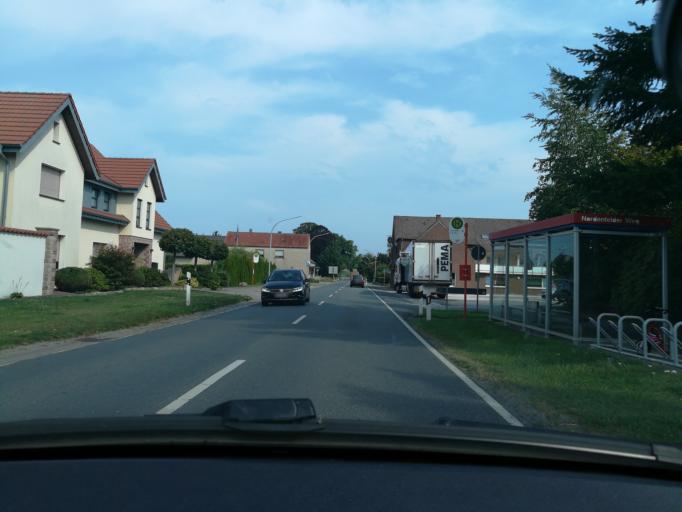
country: DE
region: Lower Saxony
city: Melle
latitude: 52.1643
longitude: 8.3333
